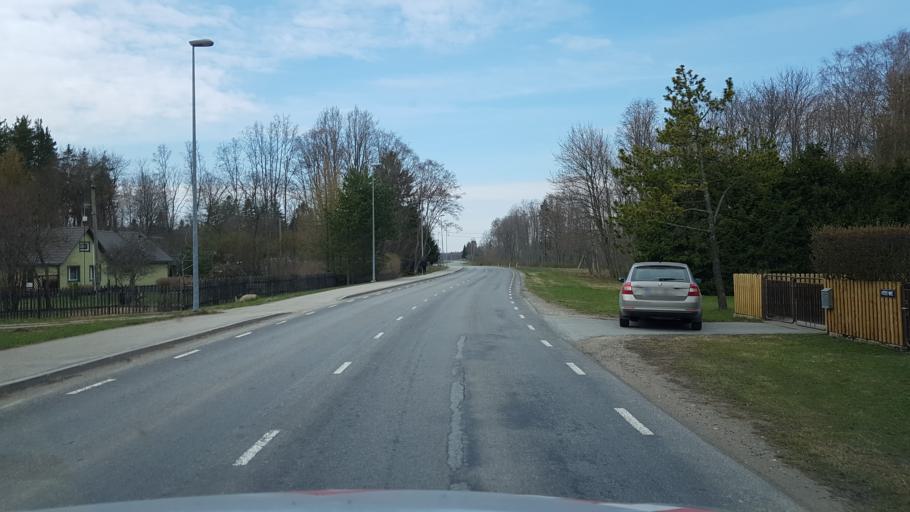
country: EE
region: Laeaene-Virumaa
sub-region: Haljala vald
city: Haljala
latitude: 59.4422
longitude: 26.2560
